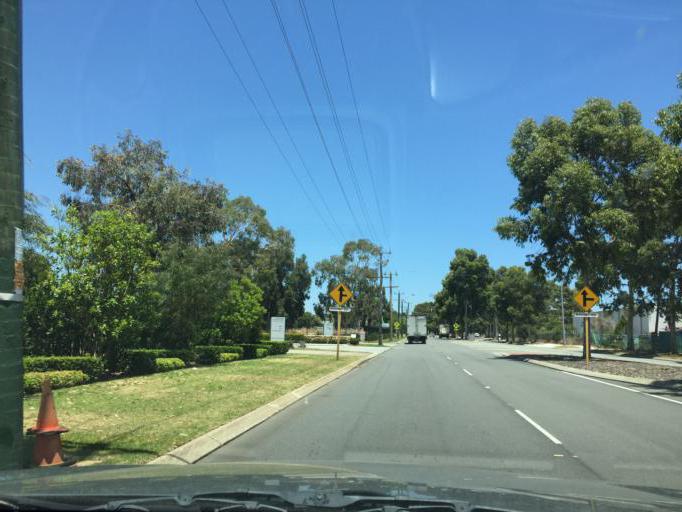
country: AU
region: Western Australia
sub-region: Canning
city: Canning Vale
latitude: -32.0610
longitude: 115.9299
